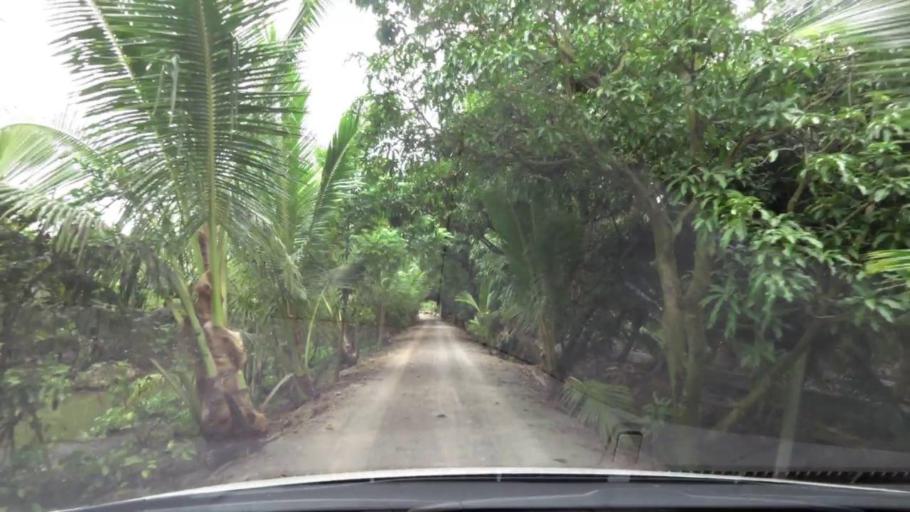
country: TH
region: Ratchaburi
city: Damnoen Saduak
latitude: 13.5519
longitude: 99.9982
